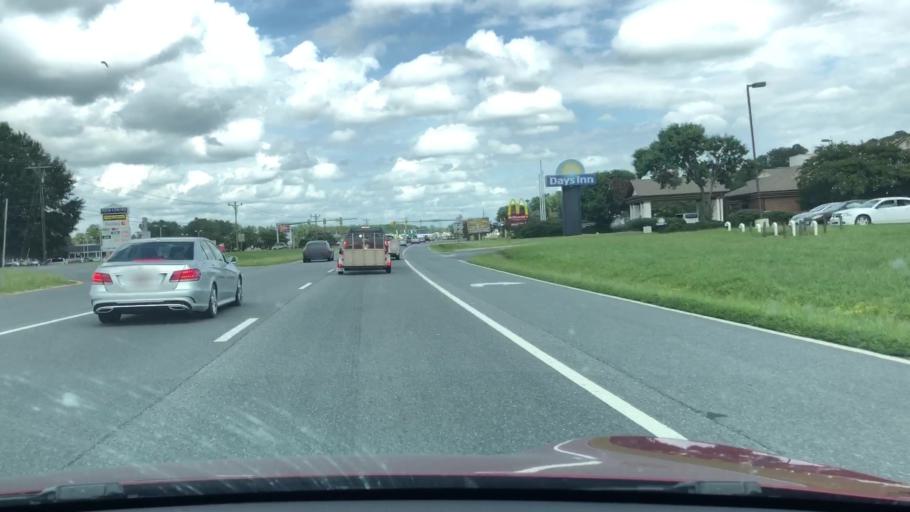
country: US
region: Virginia
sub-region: Accomack County
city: Onancock
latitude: 37.6947
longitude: -75.7198
